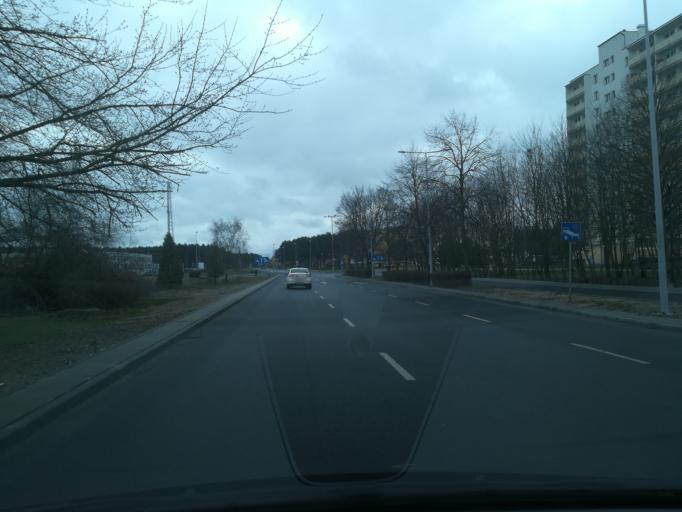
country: PL
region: Kujawsko-Pomorskie
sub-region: Powiat torunski
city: Lubicz Dolny
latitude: 53.0239
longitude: 18.6883
